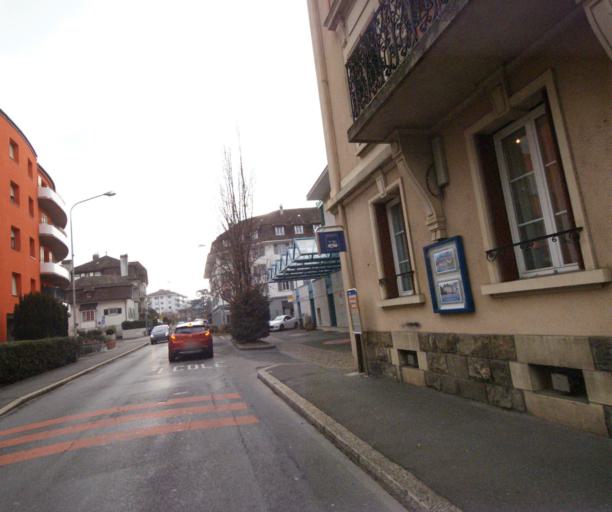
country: CH
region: Vaud
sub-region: Riviera-Pays-d'Enhaut District
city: La Tour-de-Peilz
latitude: 46.4552
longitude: 6.8583
